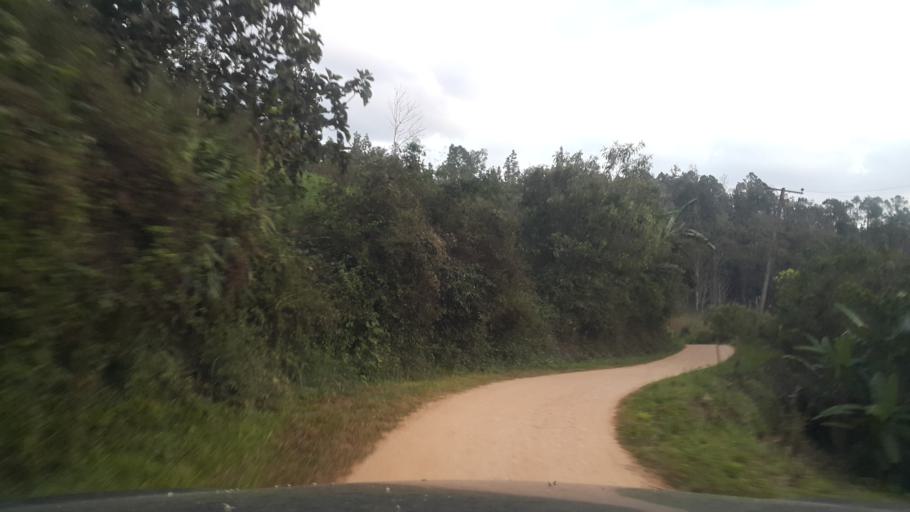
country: TH
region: Chiang Mai
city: Samoeng
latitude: 18.9530
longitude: 98.6753
